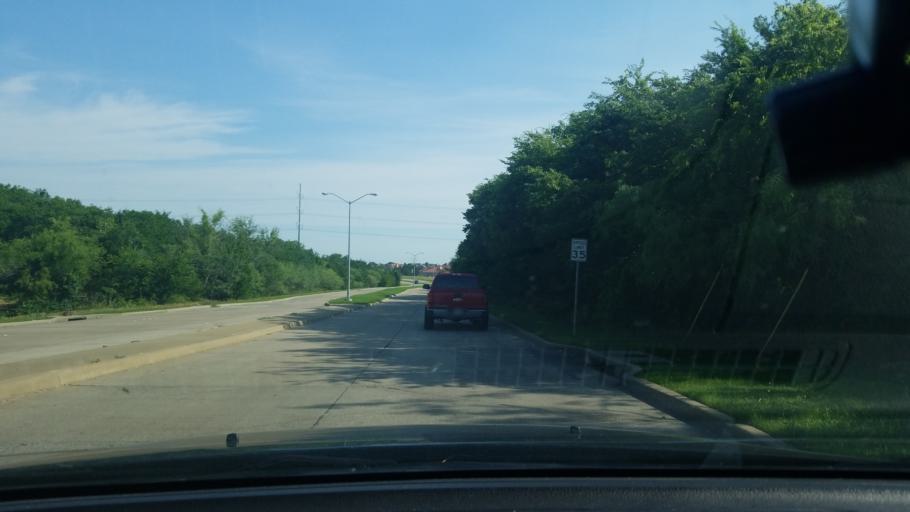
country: US
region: Texas
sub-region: Dallas County
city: Sunnyvale
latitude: 32.7729
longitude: -96.5614
